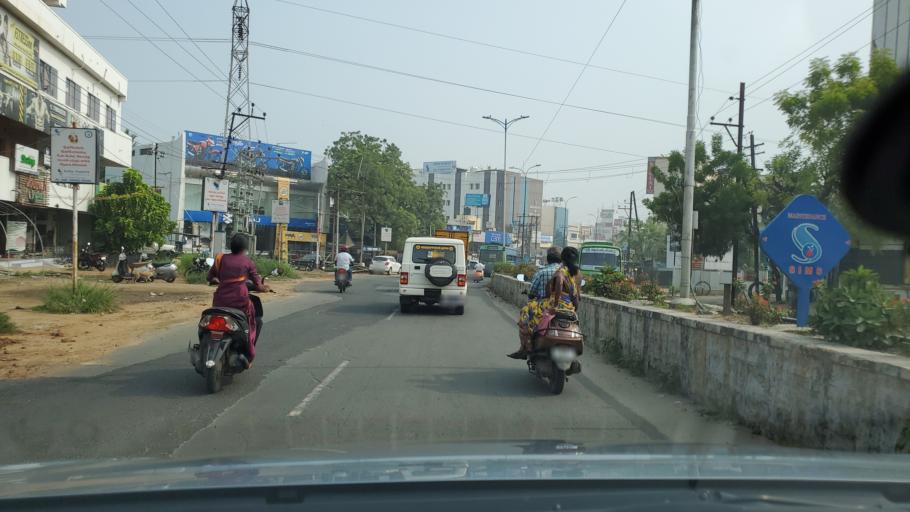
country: IN
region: Tamil Nadu
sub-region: Erode
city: Erode
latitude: 11.3361
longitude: 77.7100
